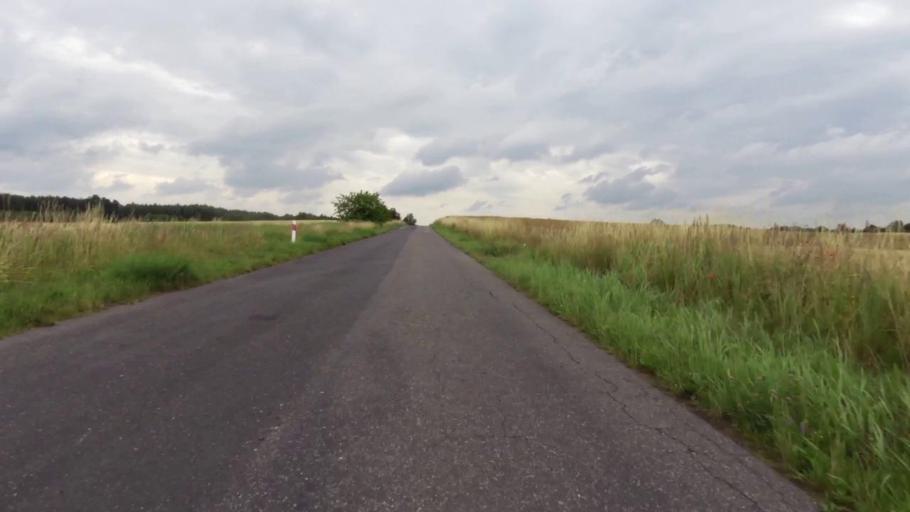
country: PL
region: West Pomeranian Voivodeship
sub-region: Powiat mysliborski
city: Mysliborz
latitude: 52.9558
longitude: 14.8810
